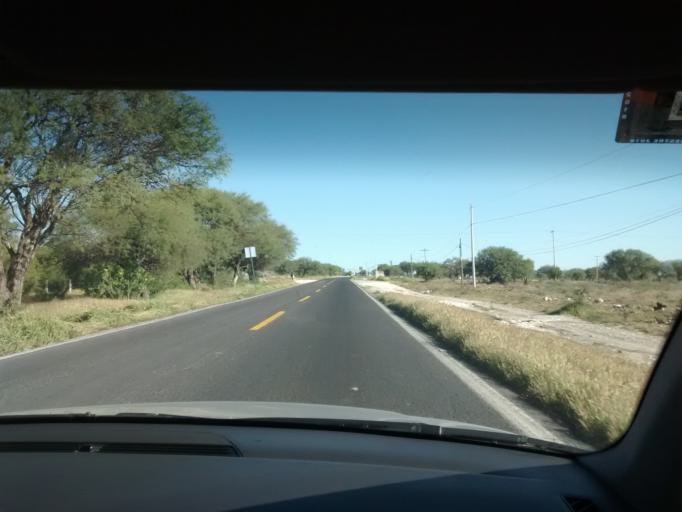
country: MX
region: Puebla
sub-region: Tepanco de Lopez
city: San Andres Cacaloapan
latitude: 18.5711
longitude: -97.5747
